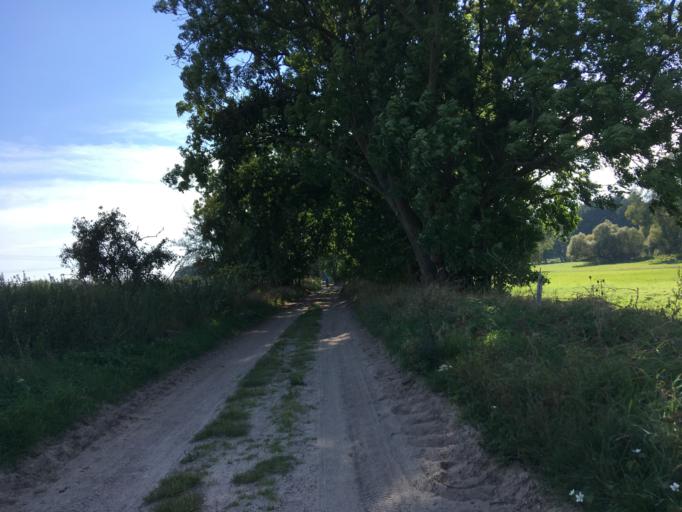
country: DE
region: Brandenburg
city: Altlandsberg
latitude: 52.5476
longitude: 13.7247
